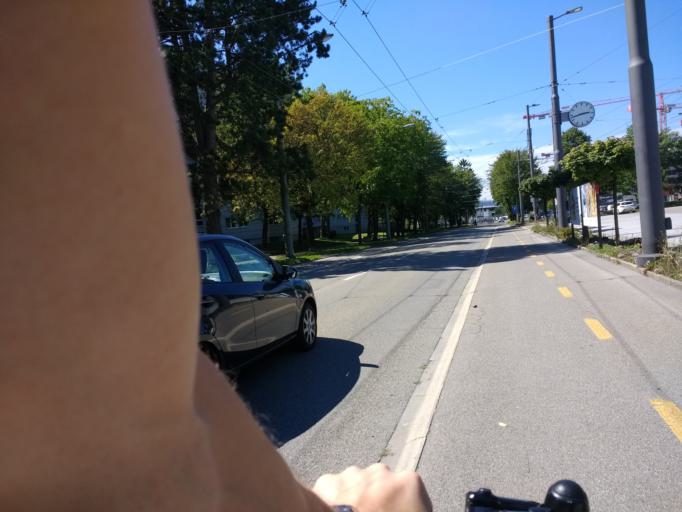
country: CH
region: Zurich
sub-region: Bezirk Winterthur
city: Mattenbach (Kreis 7) / Gutschick
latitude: 47.4938
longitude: 8.7536
